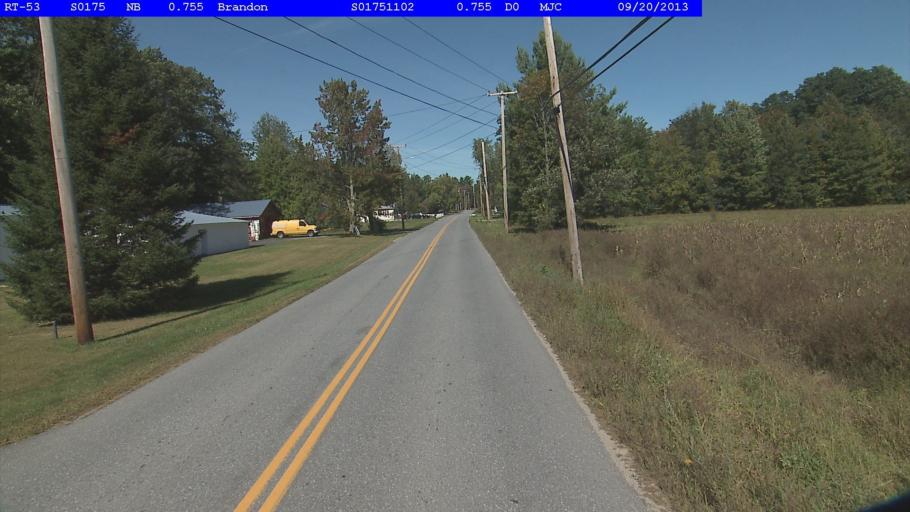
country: US
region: Vermont
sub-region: Rutland County
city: Brandon
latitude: 43.8376
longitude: -73.0561
